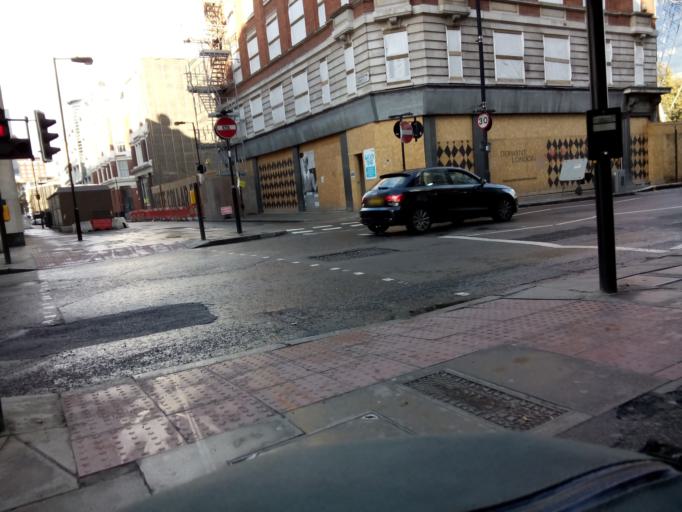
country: GB
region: England
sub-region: Greater London
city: Barbican
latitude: 51.5248
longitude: -0.0866
